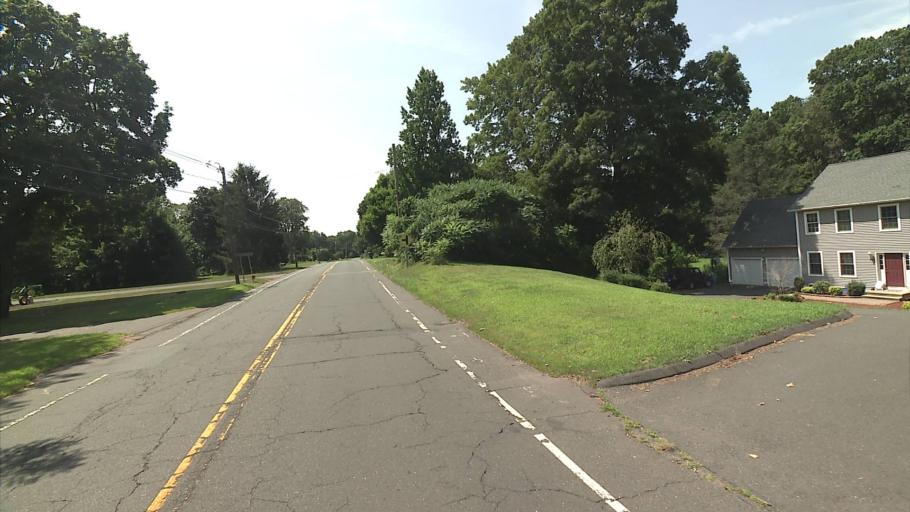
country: US
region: Connecticut
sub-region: Hartford County
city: Kensington
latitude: 41.6126
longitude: -72.7934
